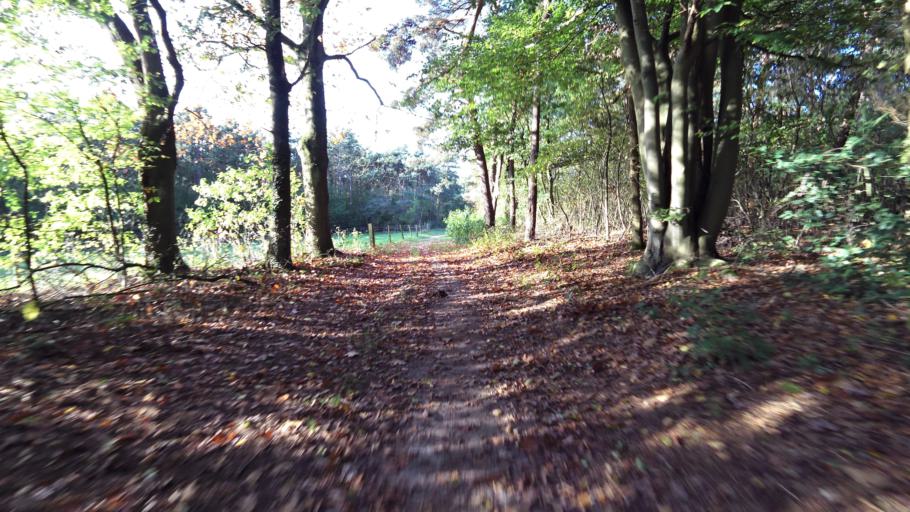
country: NL
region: Gelderland
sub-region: Gemeente Ede
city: Ede
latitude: 52.0580
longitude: 5.6639
